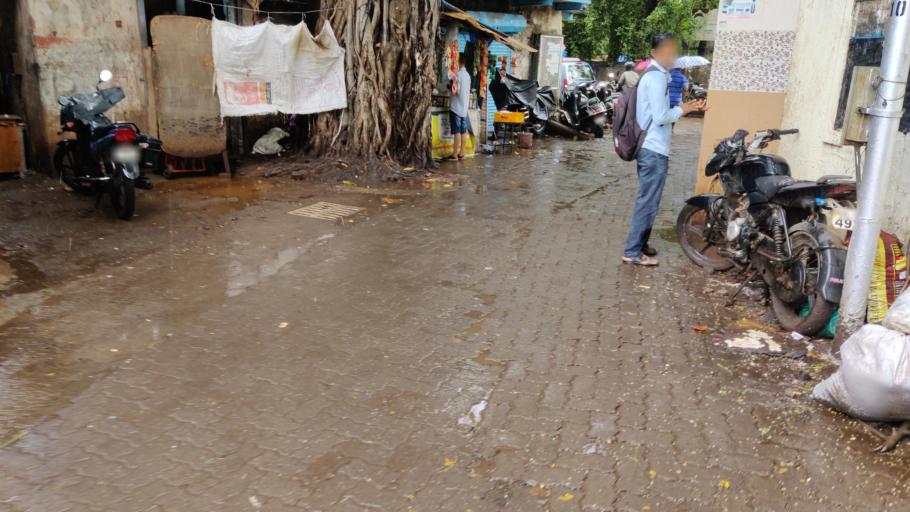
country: IN
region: Maharashtra
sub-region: Mumbai Suburban
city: Borivli
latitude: 19.2452
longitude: 72.8664
